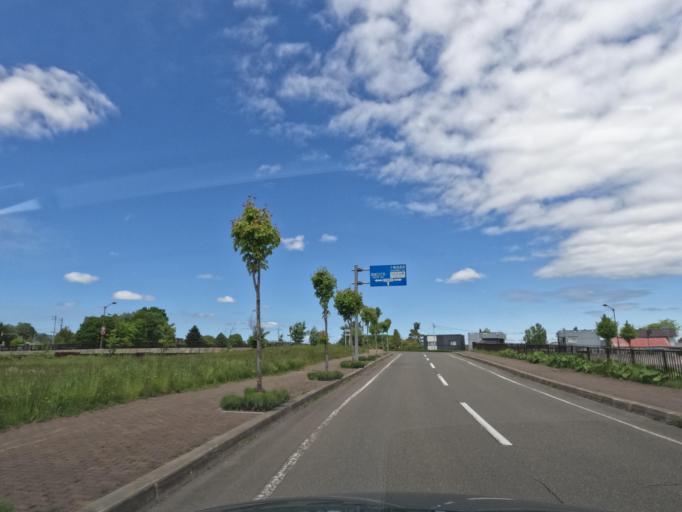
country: JP
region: Hokkaido
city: Shimo-furano
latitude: 43.4603
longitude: 142.4640
